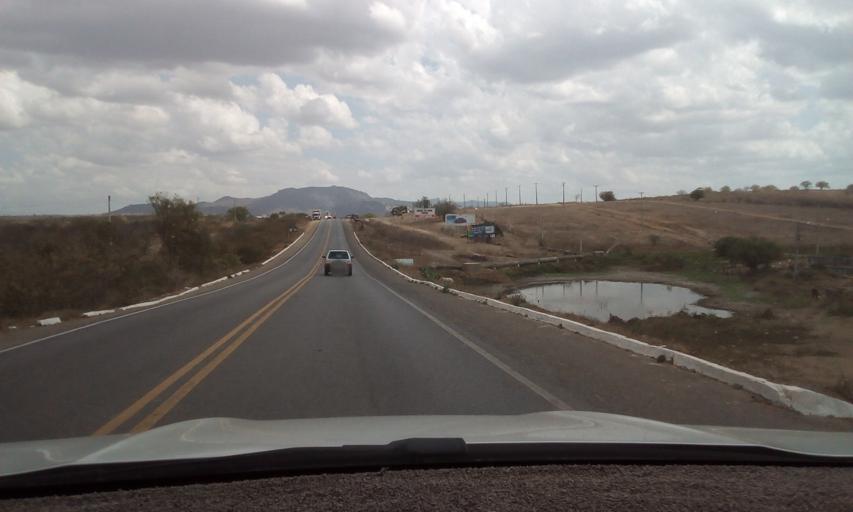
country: BR
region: Pernambuco
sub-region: Toritama
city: Toritama
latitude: -8.0218
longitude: -36.0529
